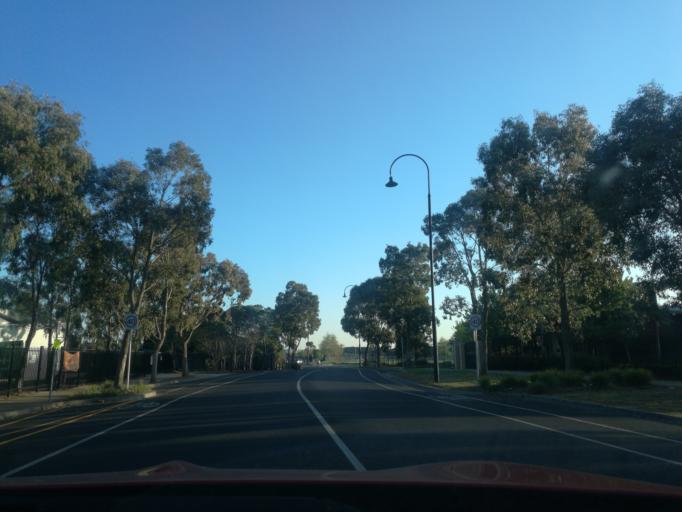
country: AU
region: Victoria
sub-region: Wyndham
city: Williams Landing
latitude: -37.8844
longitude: 144.7434
